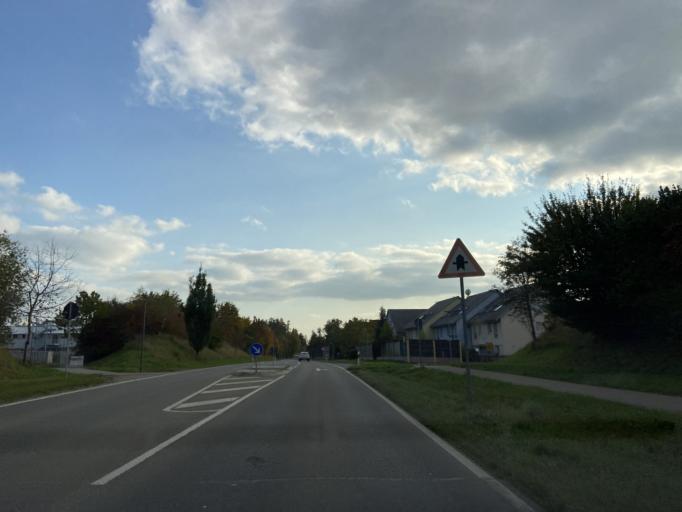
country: DE
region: Baden-Wuerttemberg
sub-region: Tuebingen Region
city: Sigmaringen
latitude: 48.0912
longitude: 9.2411
